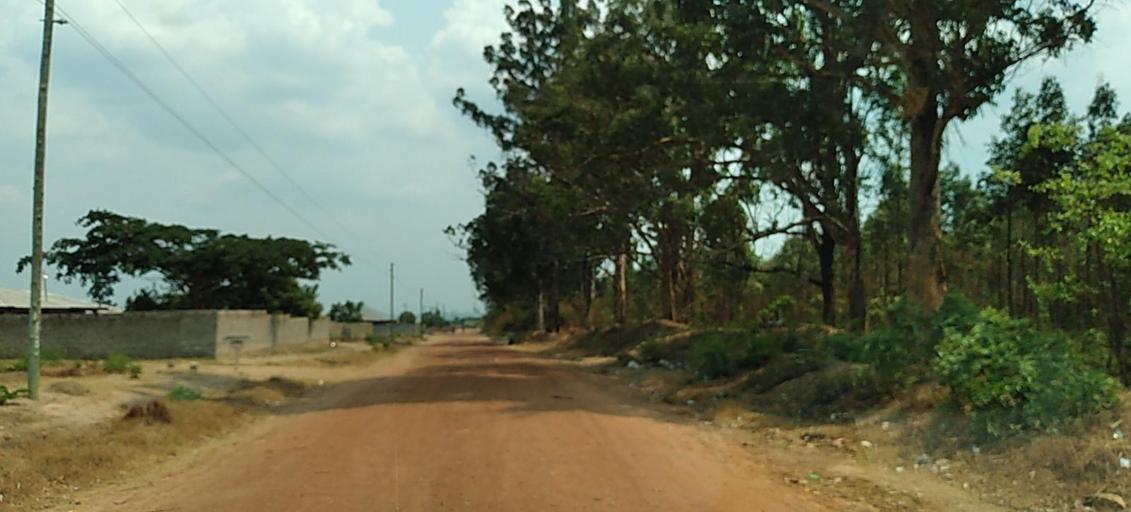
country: ZM
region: Copperbelt
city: Kalulushi
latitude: -12.8486
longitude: 28.0780
